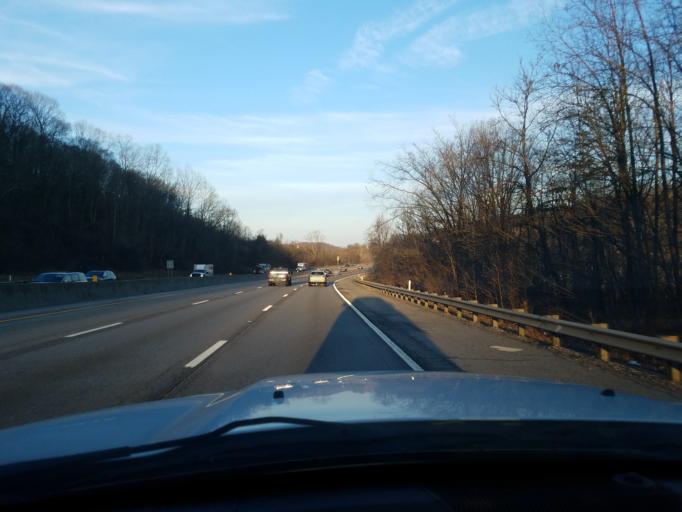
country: US
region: West Virginia
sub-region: Kanawha County
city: Nitro
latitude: 38.4283
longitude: -81.8217
